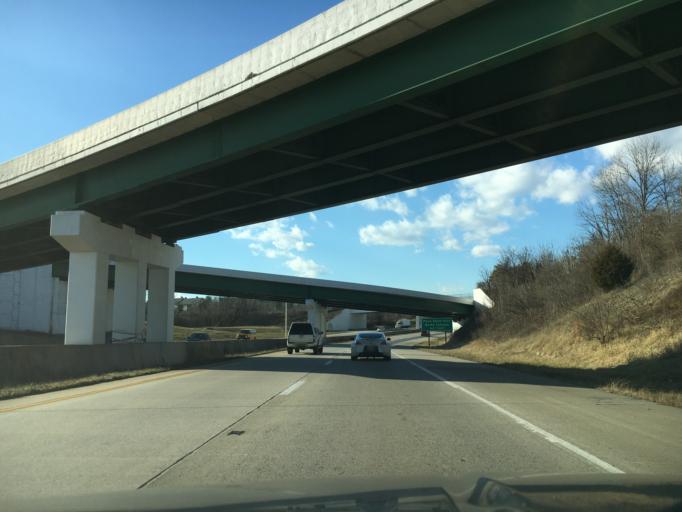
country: US
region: Pennsylvania
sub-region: Berks County
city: Wyomissing Hills
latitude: 40.3524
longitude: -75.9632
